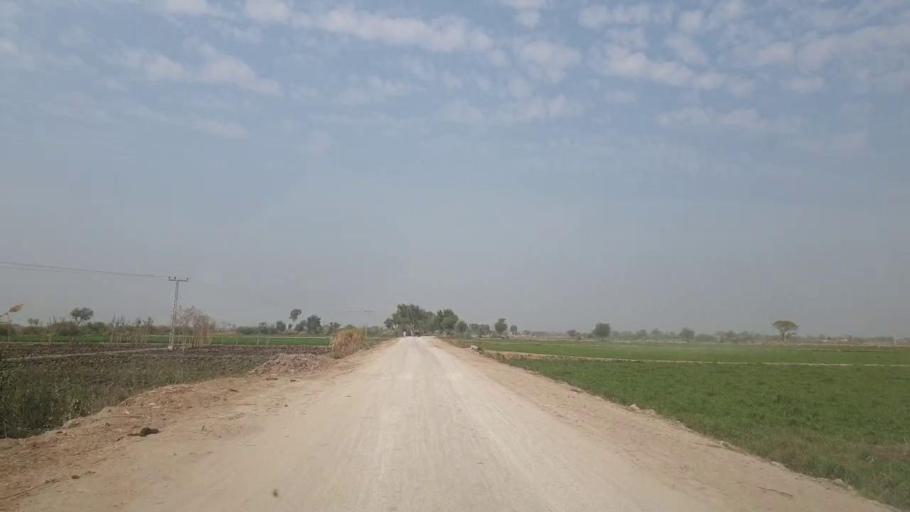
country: PK
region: Sindh
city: Mirpur Khas
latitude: 25.5465
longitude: 69.0815
